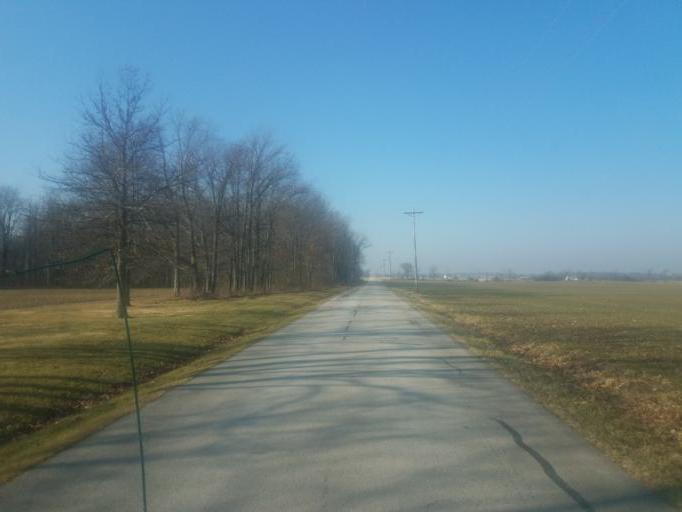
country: US
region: Ohio
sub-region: Seneca County
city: Tiffin
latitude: 41.0371
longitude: -83.0994
